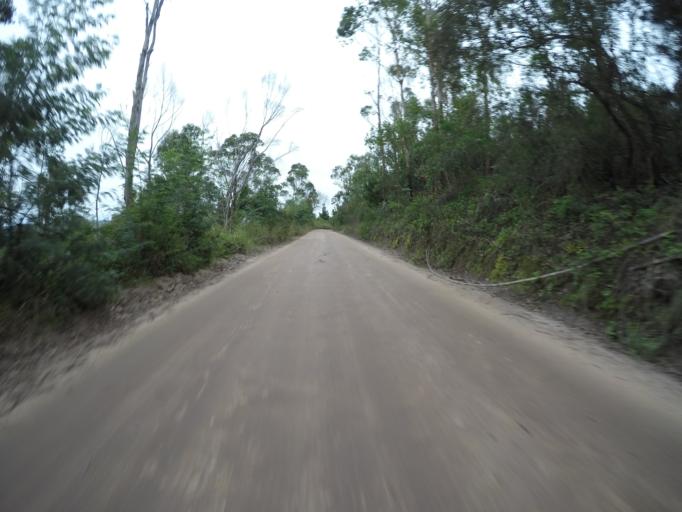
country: ZA
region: Western Cape
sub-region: Eden District Municipality
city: Knysna
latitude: -34.0074
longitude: 22.7972
